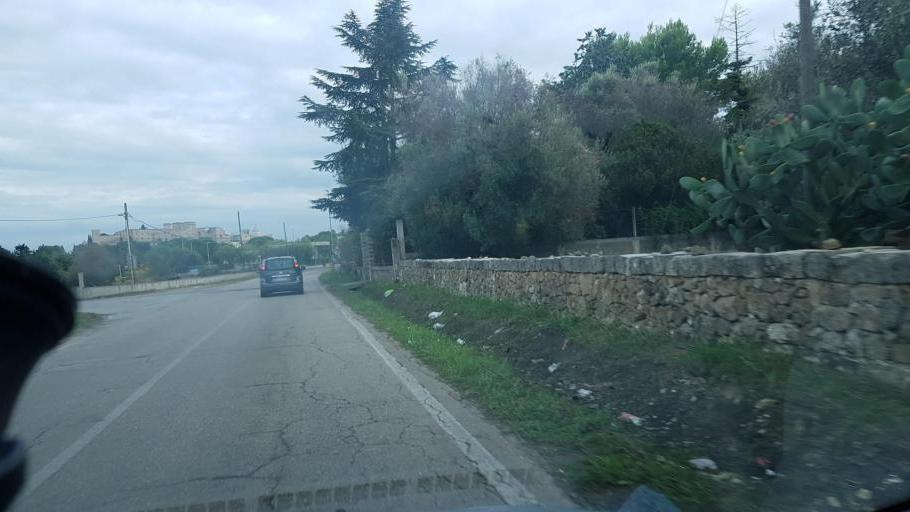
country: IT
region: Apulia
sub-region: Provincia di Brindisi
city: Oria
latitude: 40.5040
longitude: 17.6324
